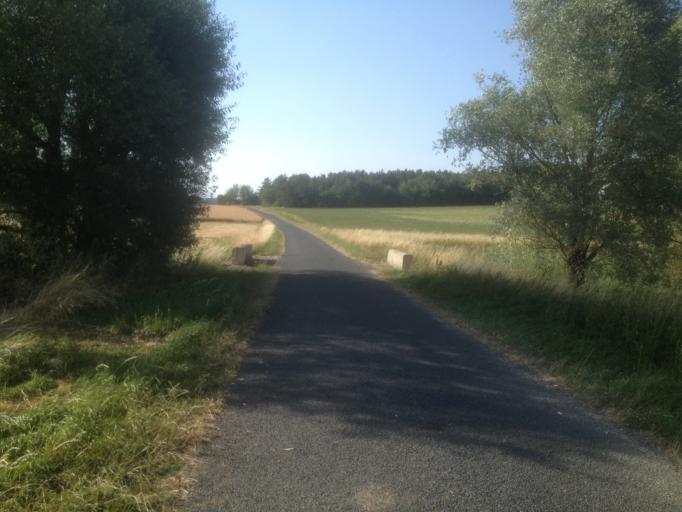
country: FR
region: Champagne-Ardenne
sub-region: Departement de la Haute-Marne
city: Doulaincourt-Saucourt
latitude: 48.4525
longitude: 5.3309
